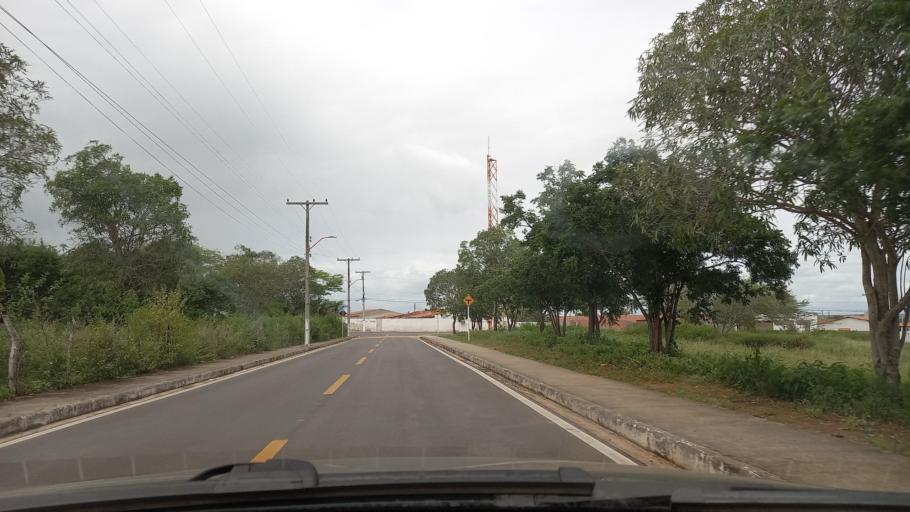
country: BR
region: Sergipe
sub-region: Caninde De Sao Francisco
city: Caninde de Sao Francisco
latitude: -9.6173
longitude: -37.7666
